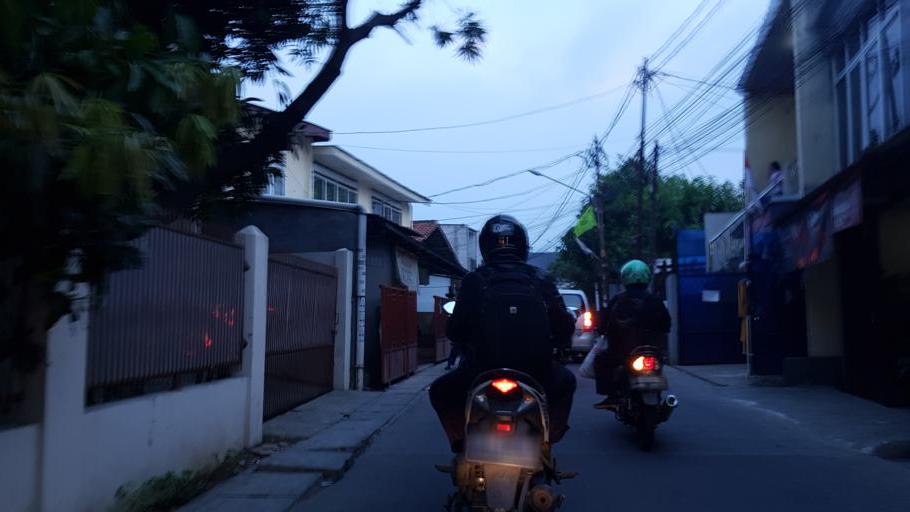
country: ID
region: West Java
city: Pamulang
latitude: -6.3234
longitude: 106.7938
